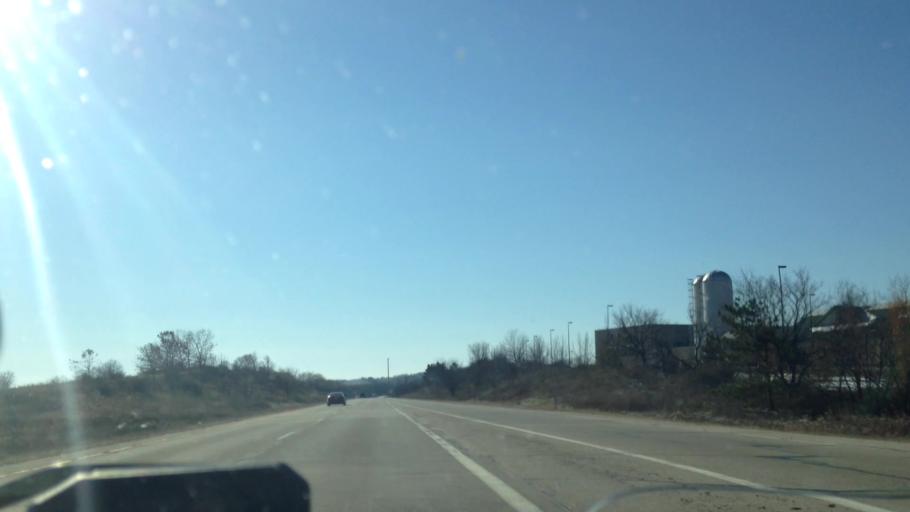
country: US
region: Wisconsin
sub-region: Washington County
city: Richfield
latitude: 43.2803
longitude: -88.1862
